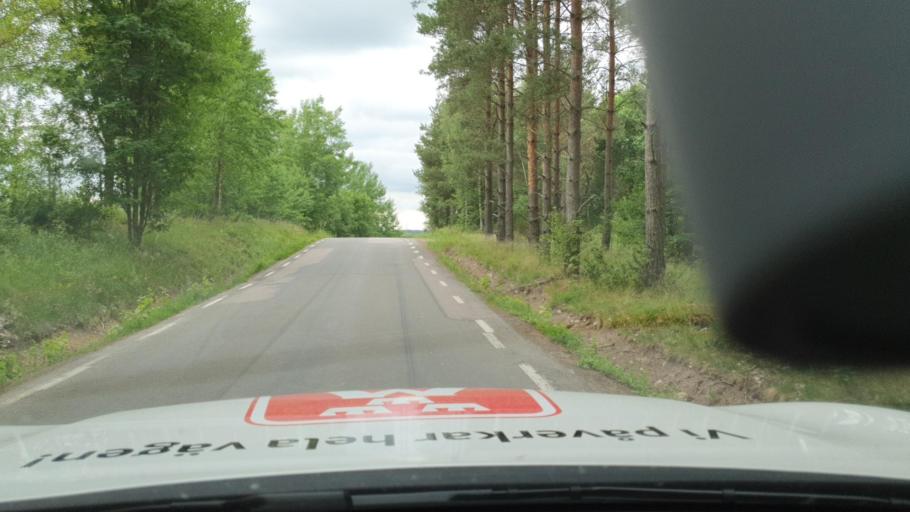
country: SE
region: Vaestra Goetaland
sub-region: Tidaholms Kommun
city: Olofstorp
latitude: 58.2814
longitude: 14.1041
